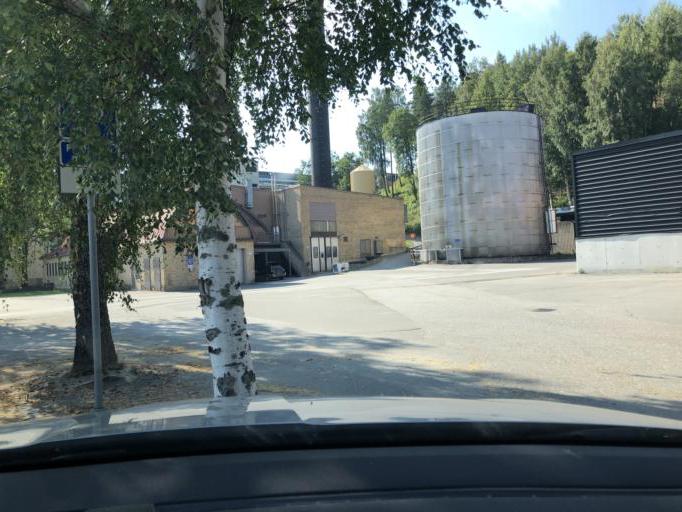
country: SE
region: Vaesternorrland
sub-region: OErnskoeldsviks Kommun
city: Ornskoldsvik
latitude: 63.3013
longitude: 18.7125
